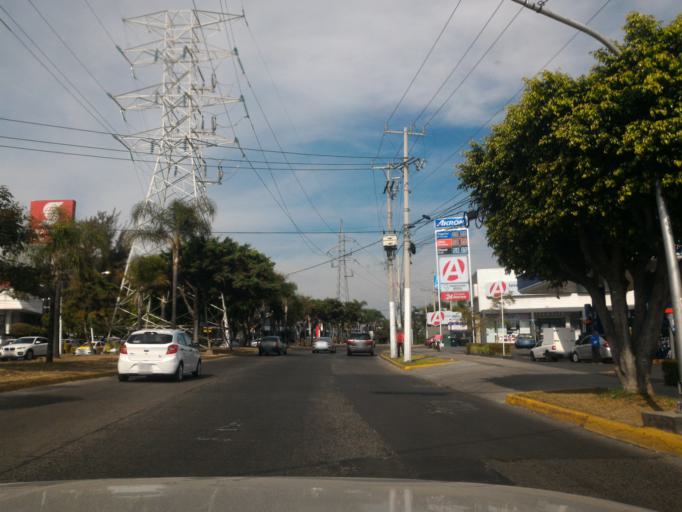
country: MX
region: Jalisco
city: Zapopan2
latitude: 20.6880
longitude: -103.4198
